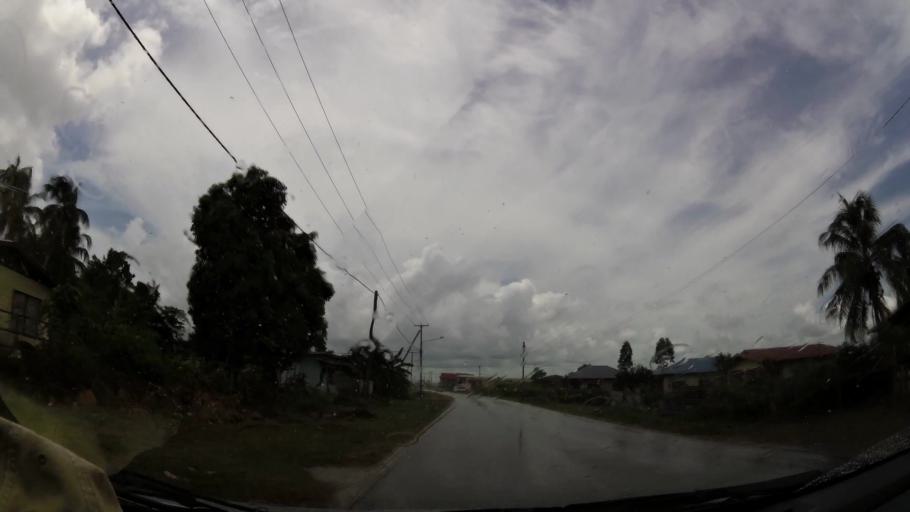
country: SR
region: Wanica
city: Lelydorp
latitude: 5.7911
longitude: -55.2208
